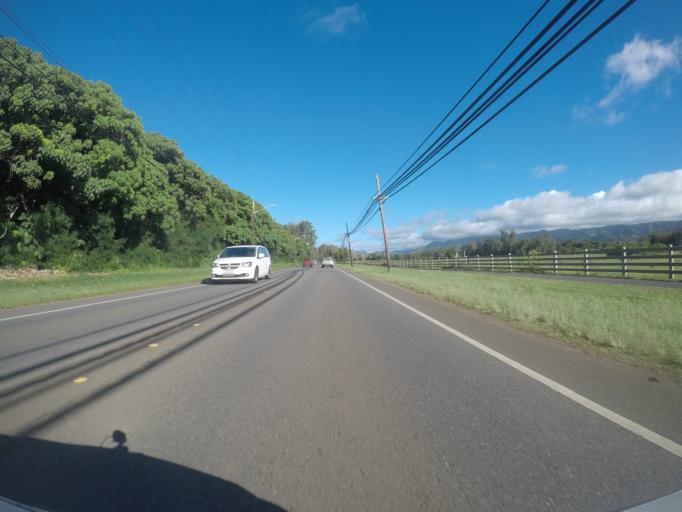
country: US
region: Hawaii
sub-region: Honolulu County
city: La'ie
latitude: 21.6598
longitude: -157.9331
